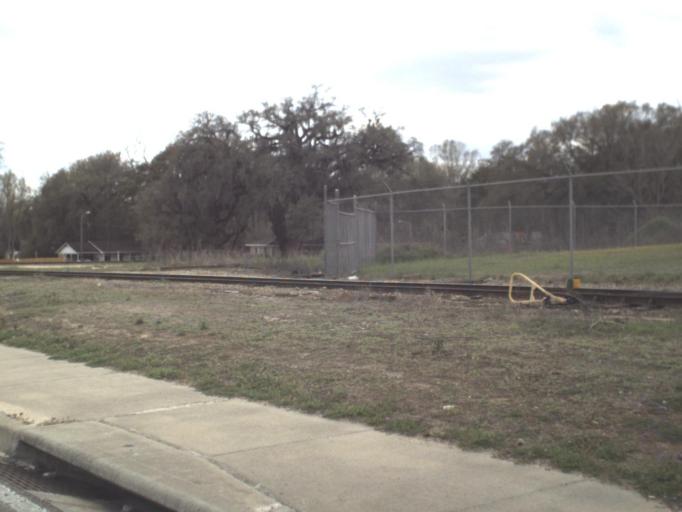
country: US
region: Florida
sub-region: Gadsden County
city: Quincy
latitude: 30.5835
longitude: -84.5915
